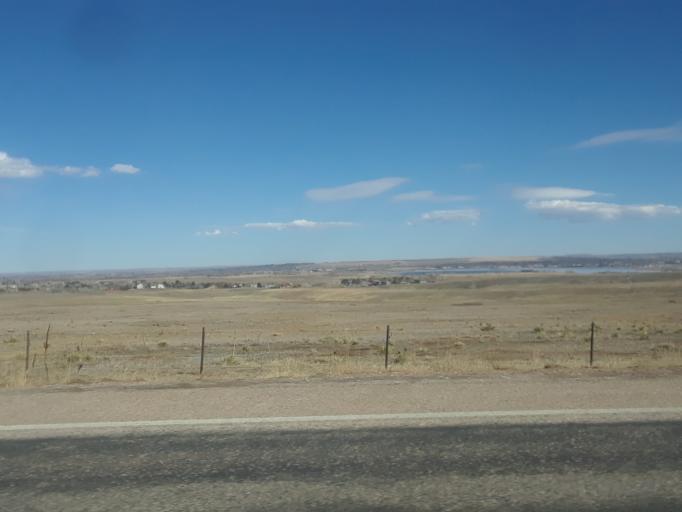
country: US
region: Colorado
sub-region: Boulder County
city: Boulder
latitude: 40.0901
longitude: -105.2822
